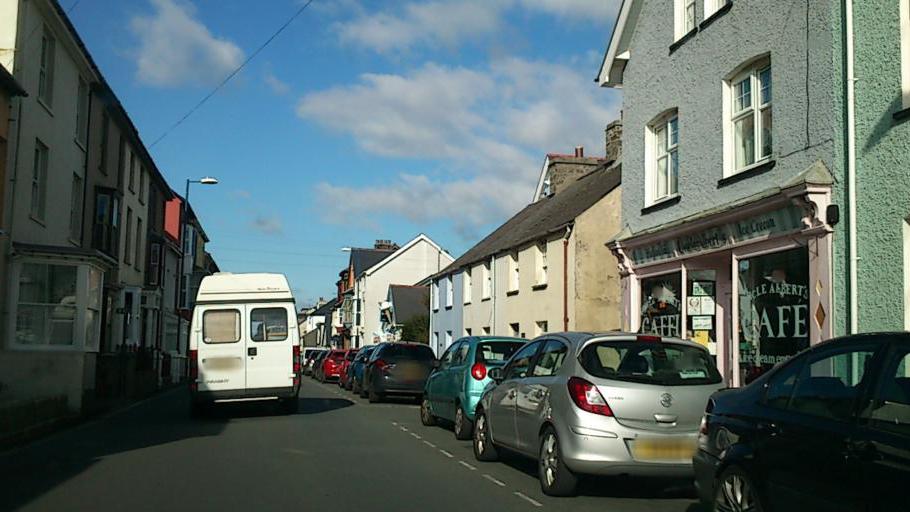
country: GB
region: Wales
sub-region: County of Ceredigion
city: Bow Street
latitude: 52.4886
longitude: -4.0514
